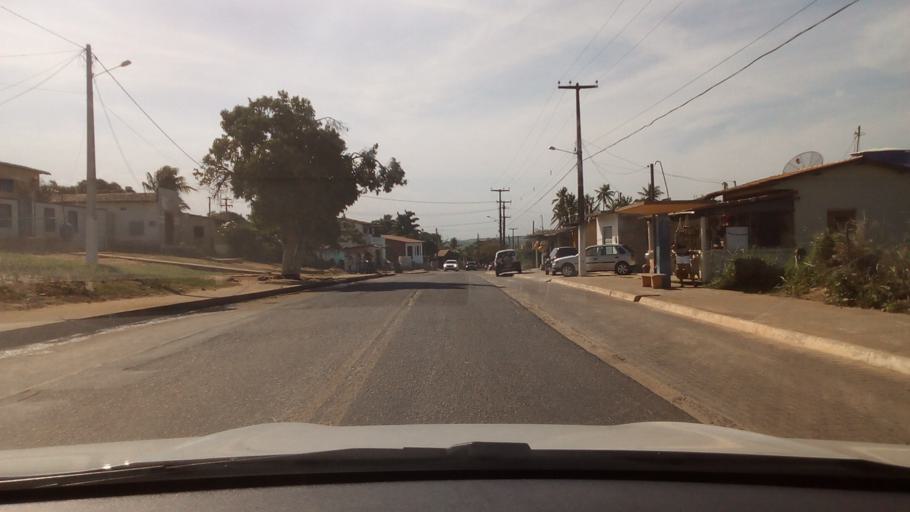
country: BR
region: Rio Grande do Norte
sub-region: Ares
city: Ares
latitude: -6.2342
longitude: -35.1585
